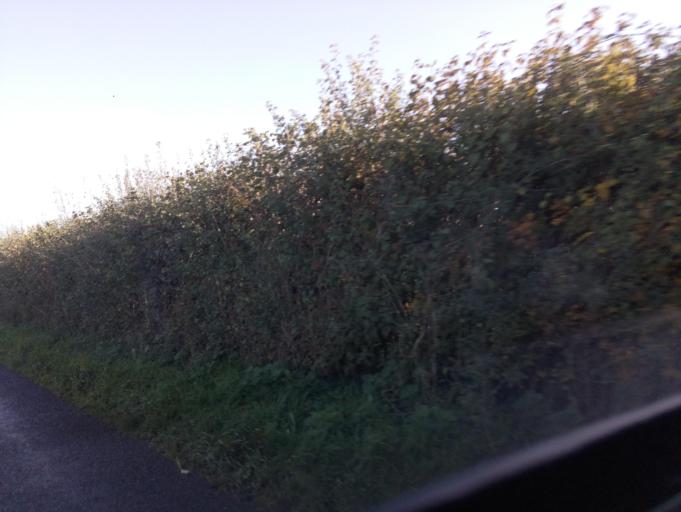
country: GB
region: England
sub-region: Somerset
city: Bruton
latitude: 51.1831
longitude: -2.4034
